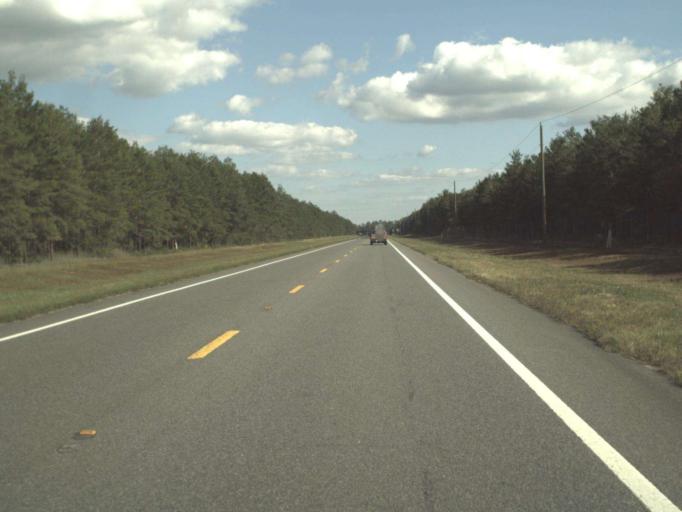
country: US
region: Florida
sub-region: Bay County
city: Lynn Haven
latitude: 30.4362
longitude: -85.6978
